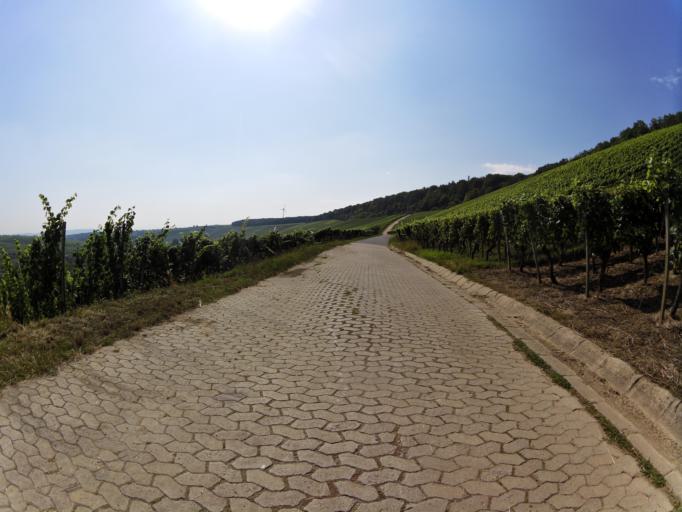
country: DE
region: Bavaria
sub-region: Regierungsbezirk Unterfranken
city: Nordheim
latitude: 49.8576
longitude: 10.1674
